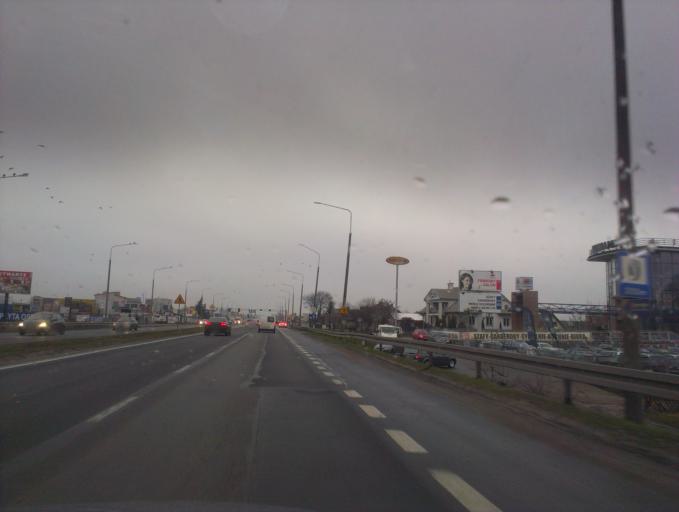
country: PL
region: Masovian Voivodeship
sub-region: Radom
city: Radom
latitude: 51.4326
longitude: 21.1486
